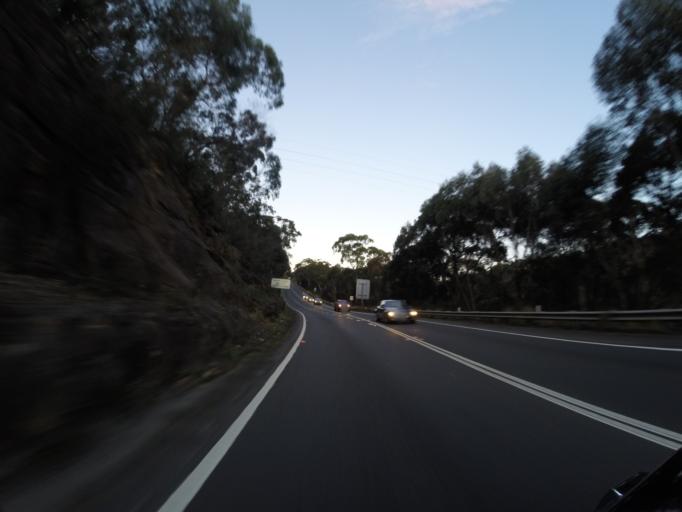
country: AU
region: New South Wales
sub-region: Sutherland Shire
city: Engadine
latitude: -34.0725
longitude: 150.9998
